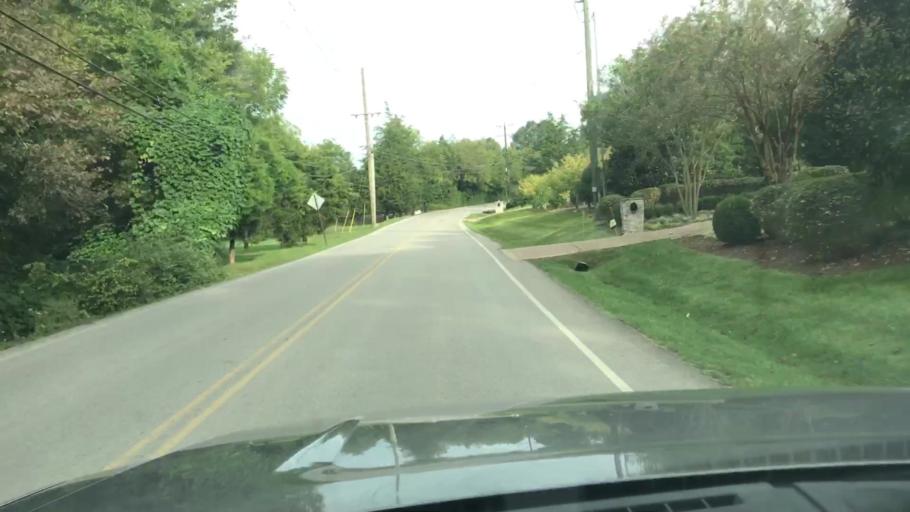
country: US
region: Tennessee
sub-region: Davidson County
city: Forest Hills
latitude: 36.0715
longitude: -86.8307
